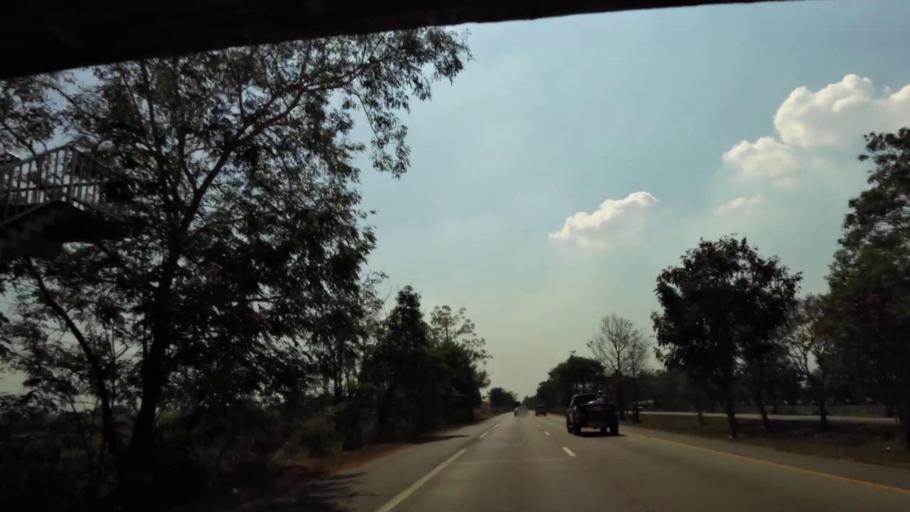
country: TH
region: Phichit
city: Wachira Barami
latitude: 16.5504
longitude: 100.1466
